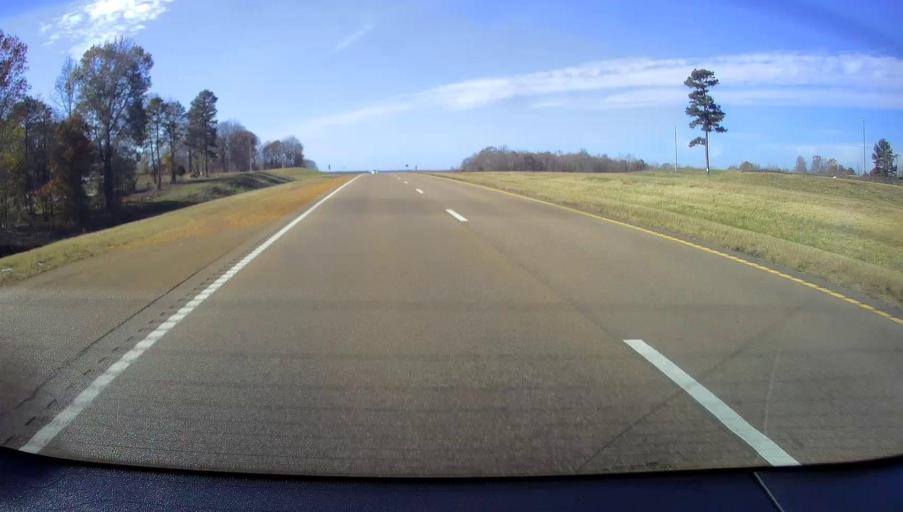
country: US
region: Mississippi
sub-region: Benton County
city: Ashland
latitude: 34.9458
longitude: -89.1812
